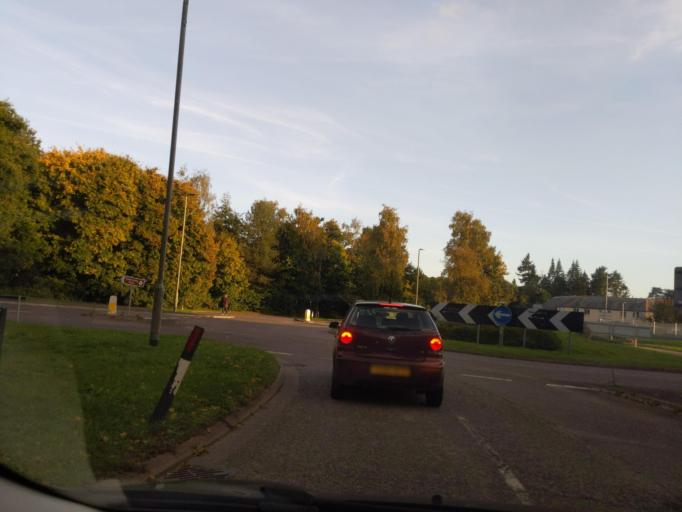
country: GB
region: England
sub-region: Devon
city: Bovey Tracey
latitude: 50.5822
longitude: -3.6723
